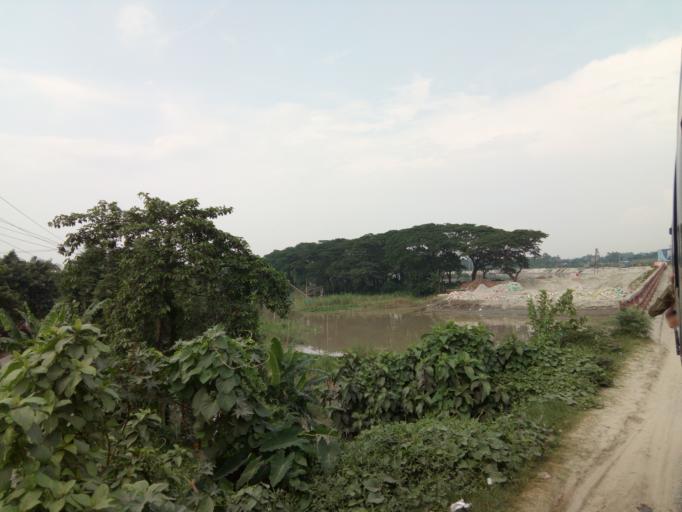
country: BD
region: Dhaka
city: Dohar
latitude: 23.5270
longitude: 90.2877
